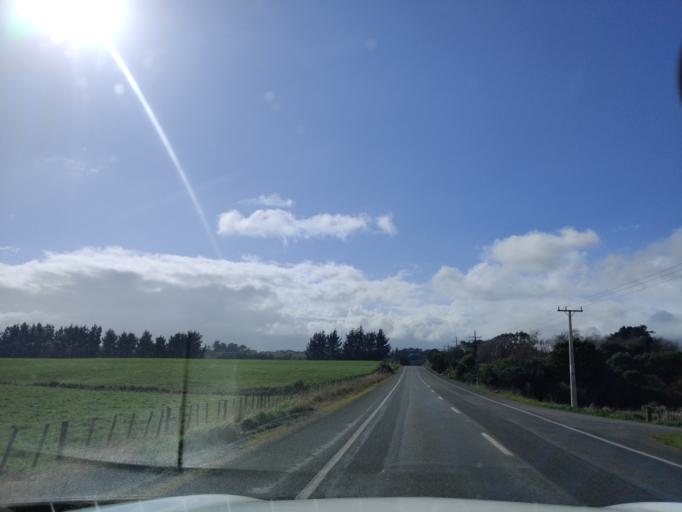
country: NZ
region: Manawatu-Wanganui
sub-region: Palmerston North City
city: Palmerston North
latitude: -40.3975
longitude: 175.6249
